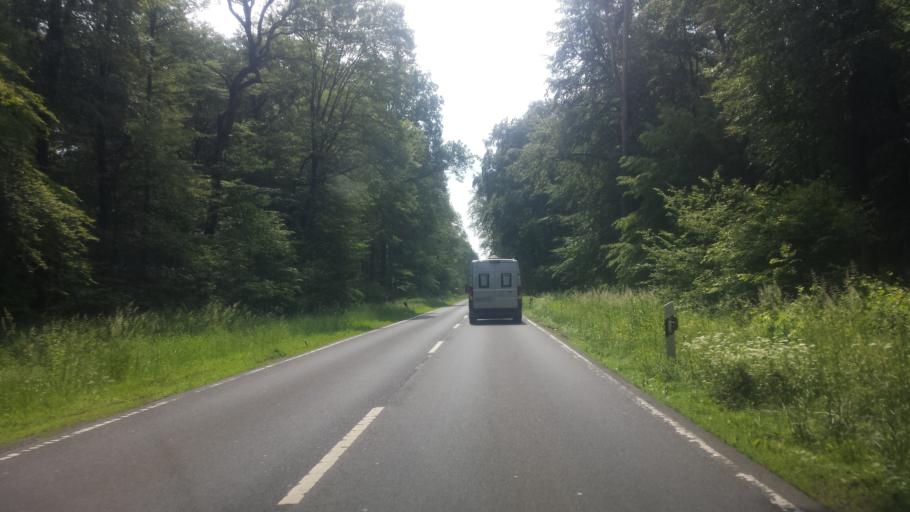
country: DE
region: Hesse
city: Dreieich
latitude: 50.0256
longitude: 8.7223
